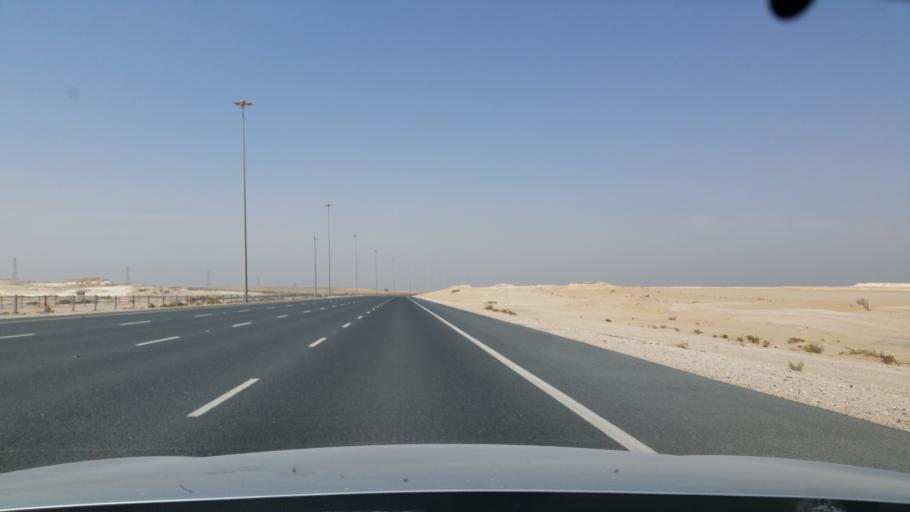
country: QA
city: Umm Bab
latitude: 24.8565
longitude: 50.8955
